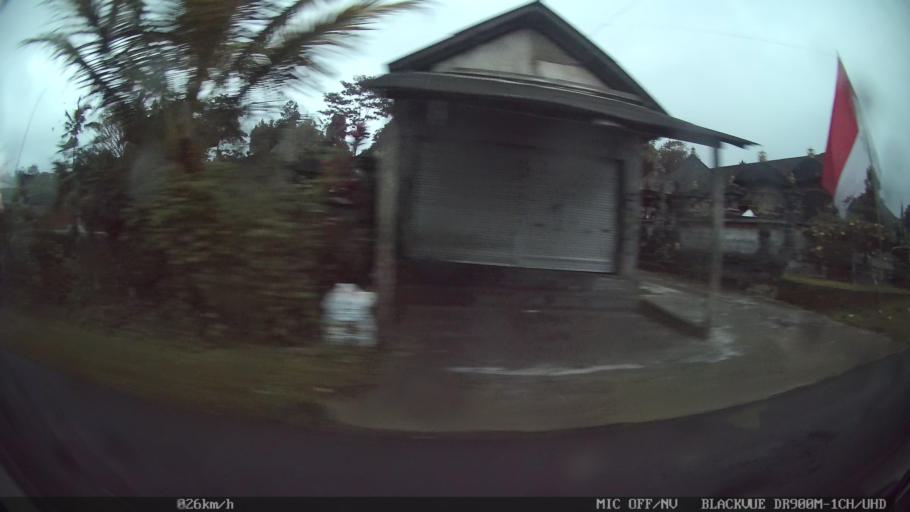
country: ID
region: Bali
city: Banjar Ponggang
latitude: -8.3887
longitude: 115.2612
